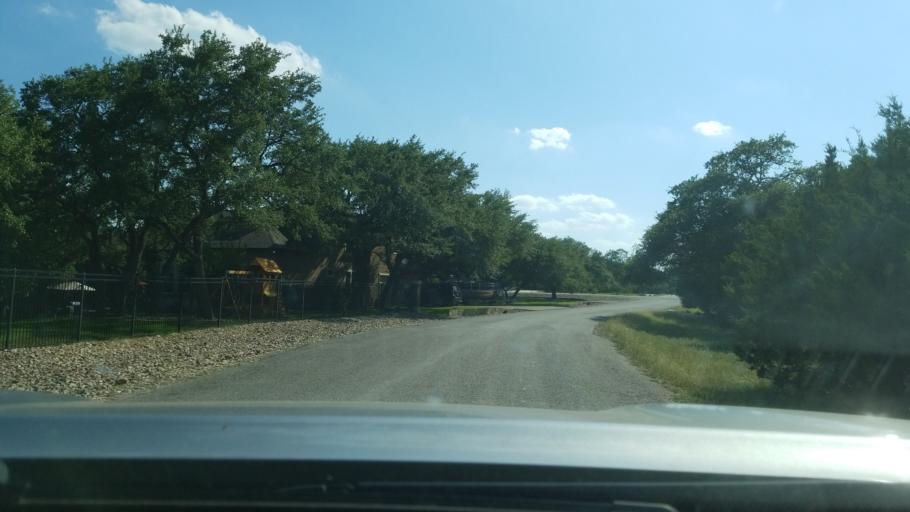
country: US
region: Texas
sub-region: Comal County
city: Bulverde
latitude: 29.8287
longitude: -98.4018
